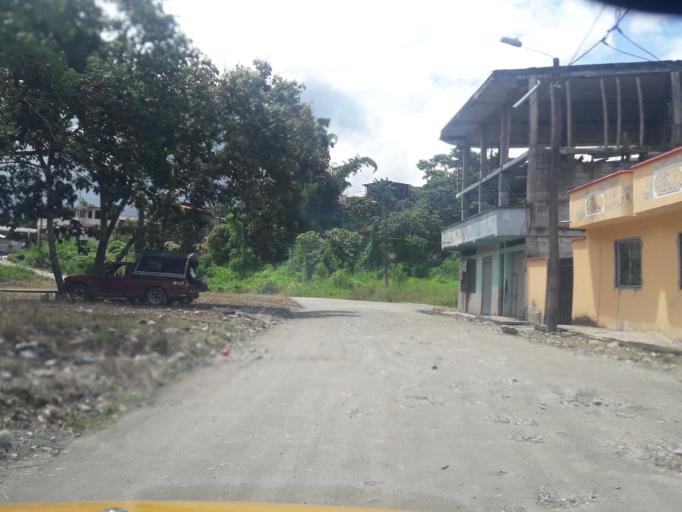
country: EC
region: Napo
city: Tena
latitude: -1.0027
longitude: -77.8157
